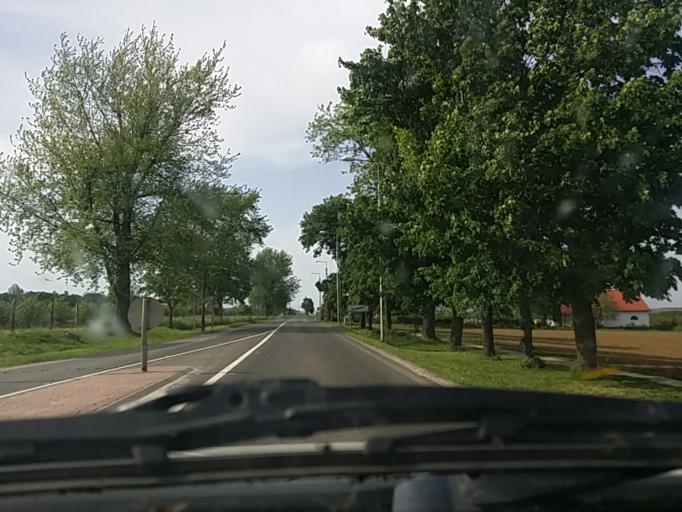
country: HU
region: Baranya
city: Kozarmisleny
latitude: 45.9571
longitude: 18.2347
